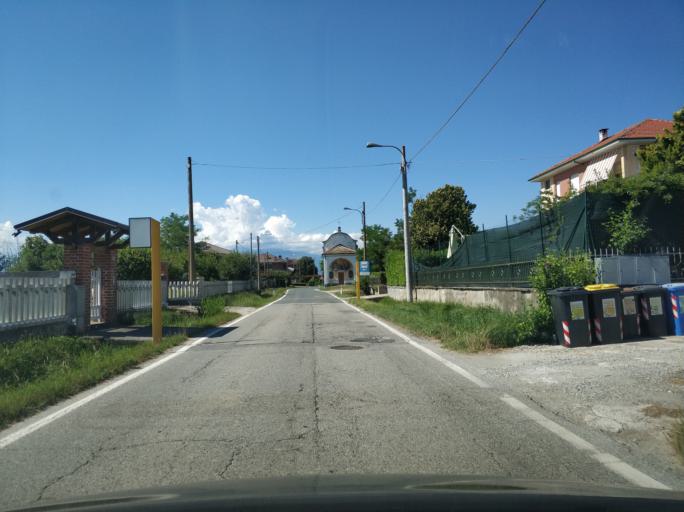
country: IT
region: Piedmont
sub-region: Provincia di Torino
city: San Benigno Canavese
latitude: 45.2350
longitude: 7.7743
